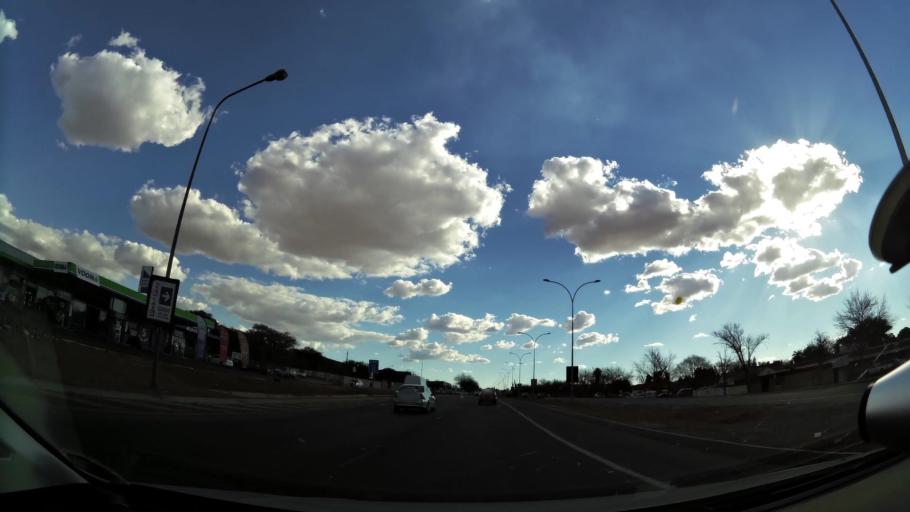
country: ZA
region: North-West
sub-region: Dr Kenneth Kaunda District Municipality
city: Klerksdorp
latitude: -26.8646
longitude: 26.6503
